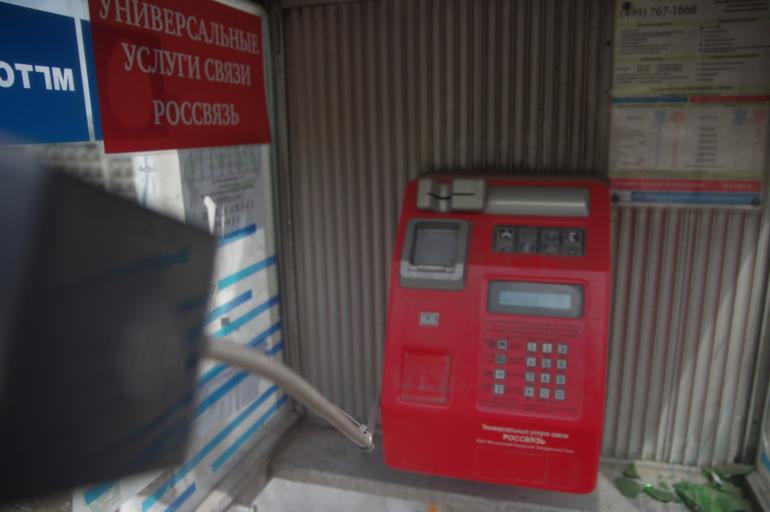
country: RU
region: Moscow
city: Novokhovrino
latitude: 55.8693
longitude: 37.5068
